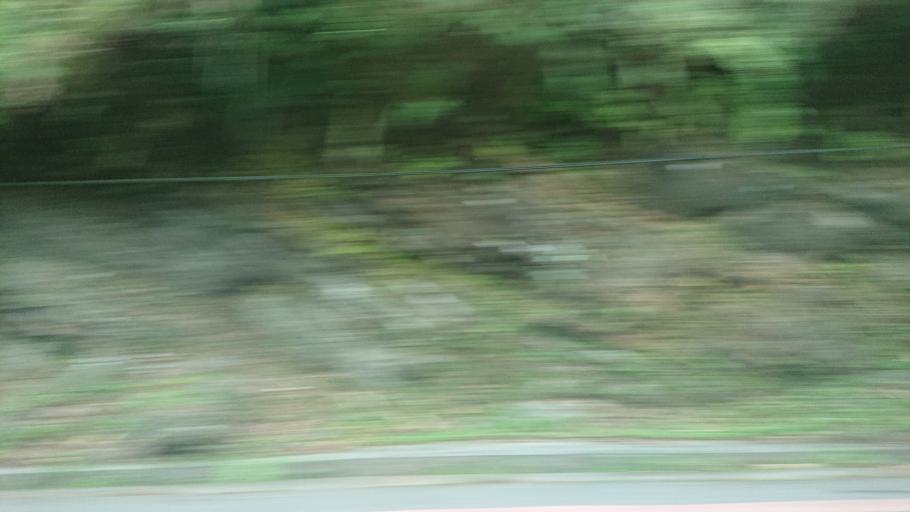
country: TW
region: Taiwan
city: Daxi
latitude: 24.8745
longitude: 121.3861
